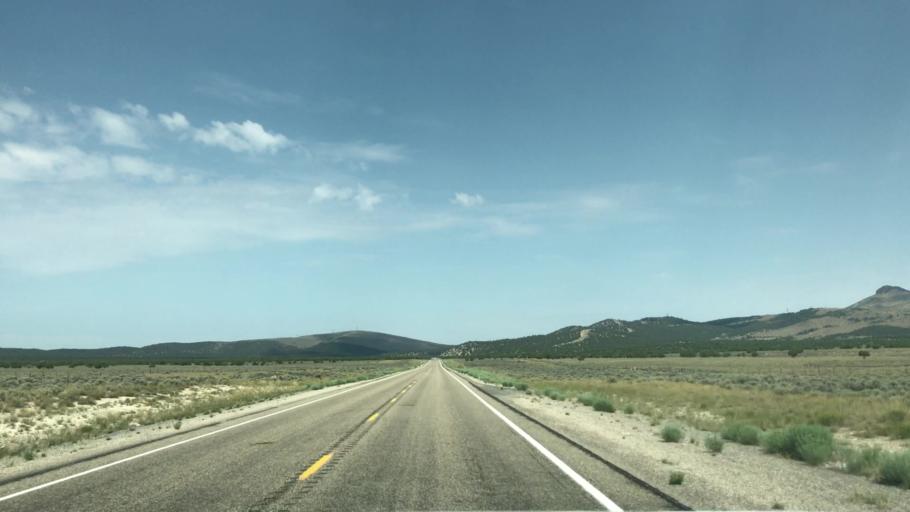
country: US
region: Nevada
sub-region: White Pine County
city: Ely
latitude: 39.3631
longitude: -115.0502
